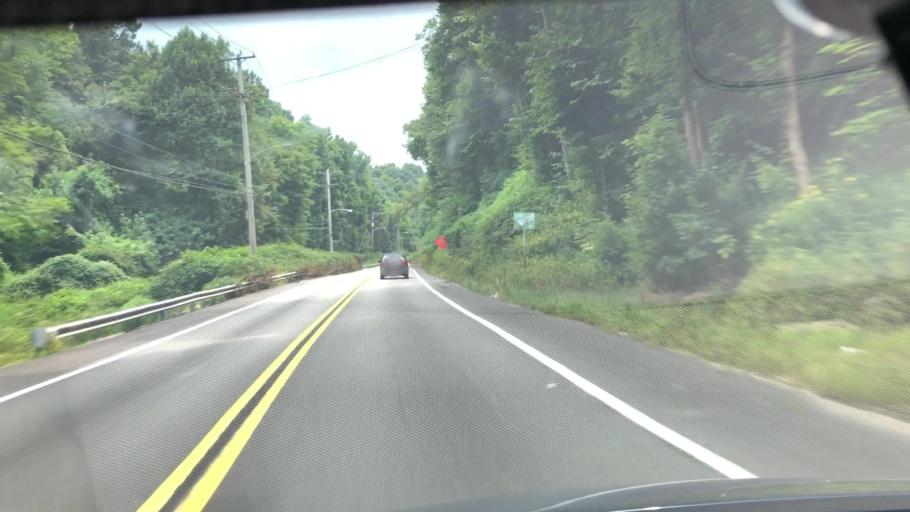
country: US
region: Pennsylvania
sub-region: Allegheny County
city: Blawnox
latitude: 40.4703
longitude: -79.8475
